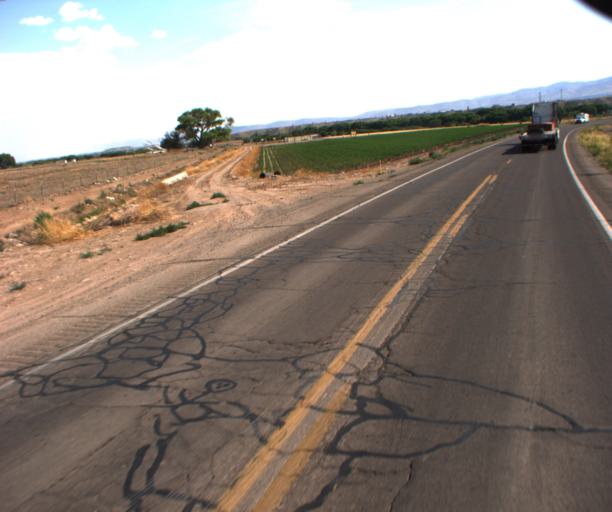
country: US
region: Arizona
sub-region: Greenlee County
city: Clifton
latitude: 32.7290
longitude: -109.0940
